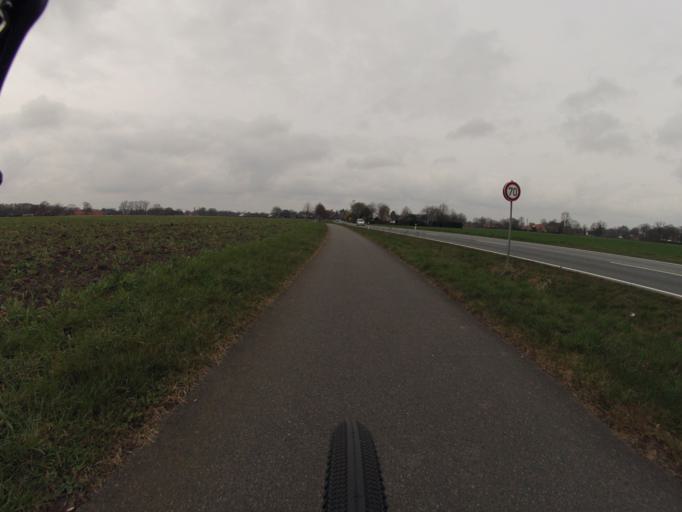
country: DE
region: North Rhine-Westphalia
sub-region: Regierungsbezirk Munster
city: Recke
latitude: 52.3477
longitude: 7.7316
